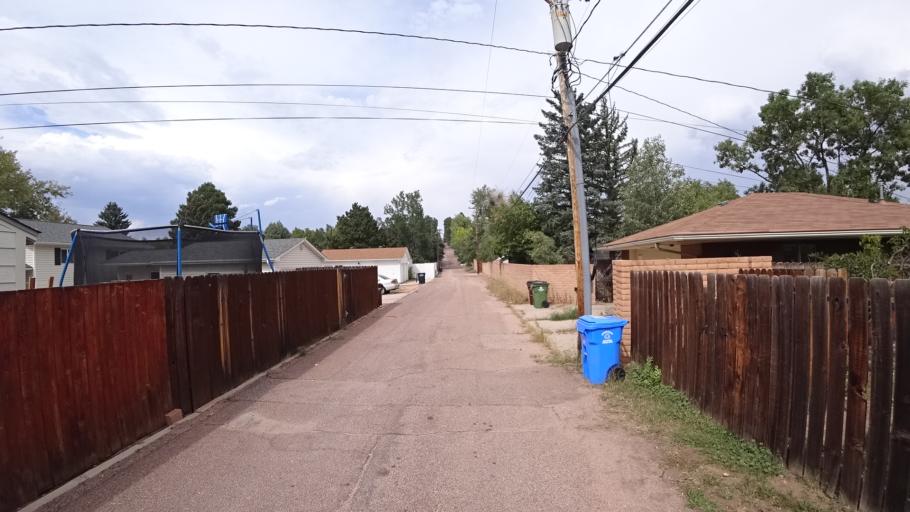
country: US
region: Colorado
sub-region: El Paso County
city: Colorado Springs
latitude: 38.8616
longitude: -104.7856
